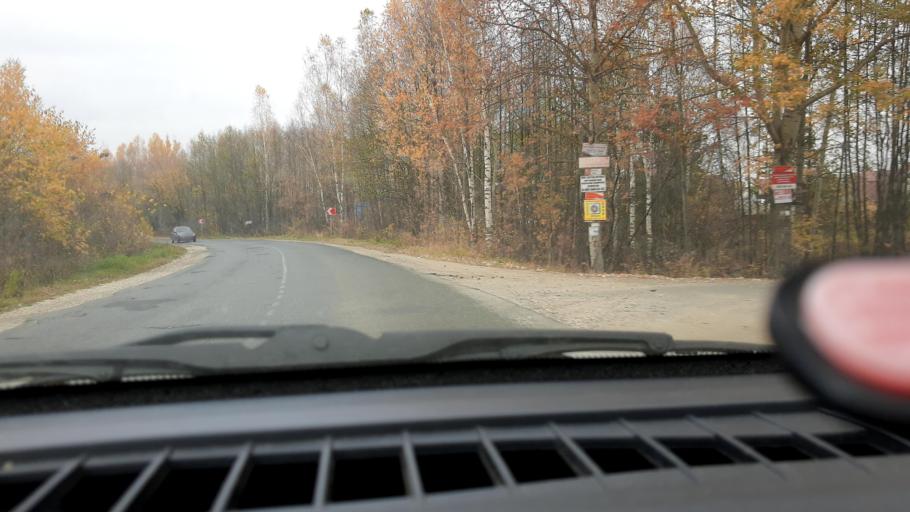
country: RU
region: Nizjnij Novgorod
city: Neklyudovo
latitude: 56.4255
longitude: 43.9259
